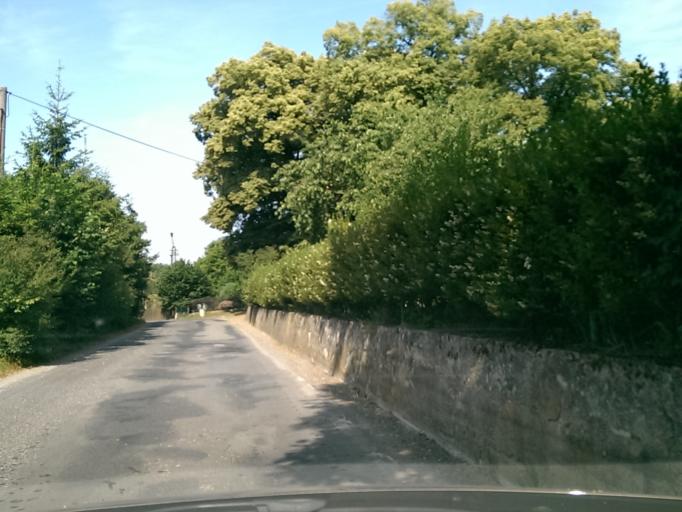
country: CZ
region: Central Bohemia
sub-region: Okres Mlada Boleslav
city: Zd'ar
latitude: 50.5118
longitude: 15.0780
